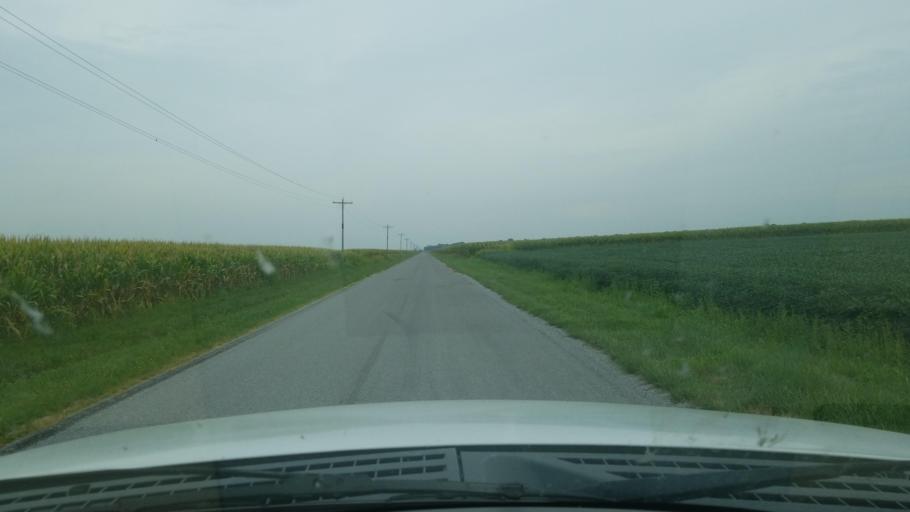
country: US
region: Illinois
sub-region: Saline County
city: Eldorado
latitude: 37.8667
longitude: -88.4726
